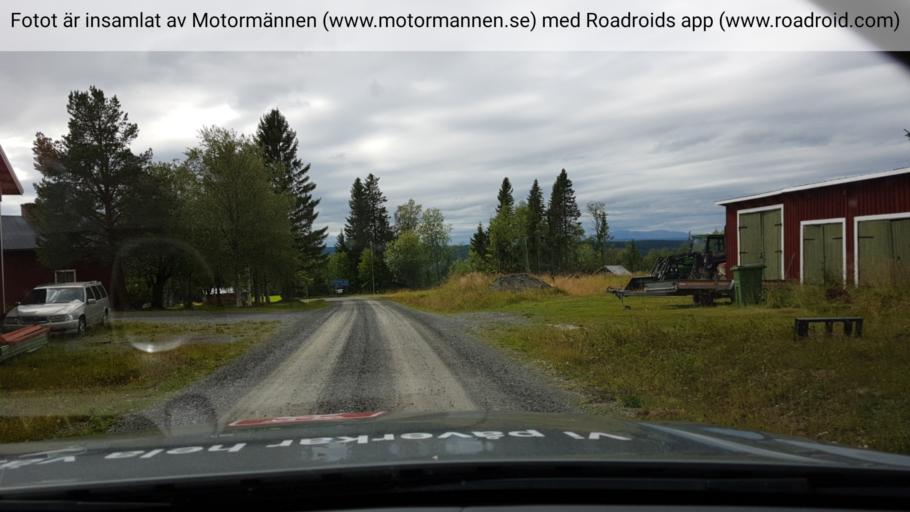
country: SE
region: Jaemtland
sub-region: Krokoms Kommun
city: Valla
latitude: 63.5219
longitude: 13.8922
